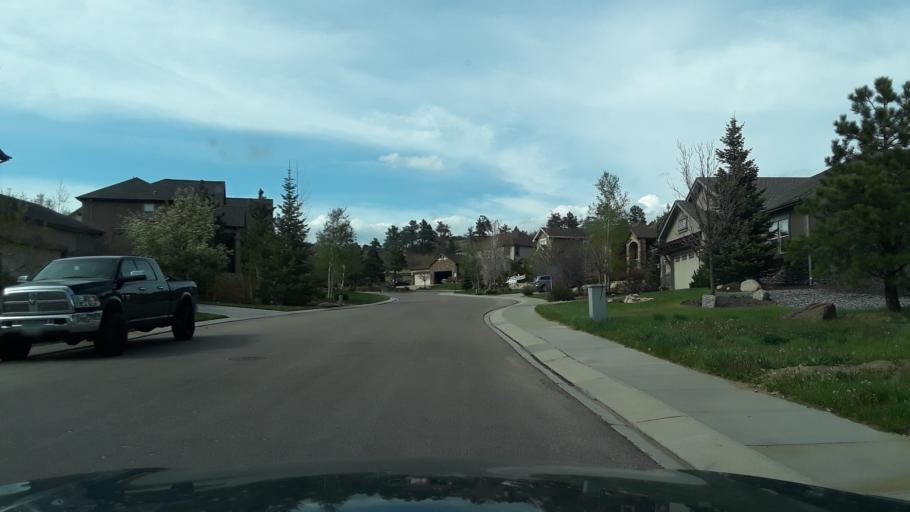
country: US
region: Colorado
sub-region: El Paso County
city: Gleneagle
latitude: 39.0150
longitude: -104.7942
